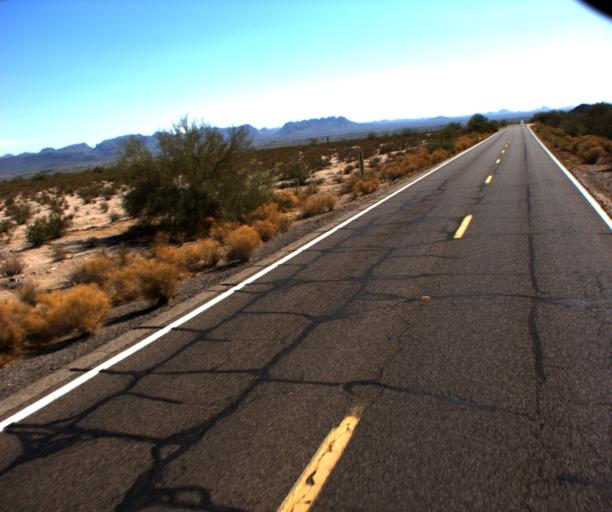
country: US
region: Arizona
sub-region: Pinal County
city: Sacaton
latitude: 33.0442
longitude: -111.7210
